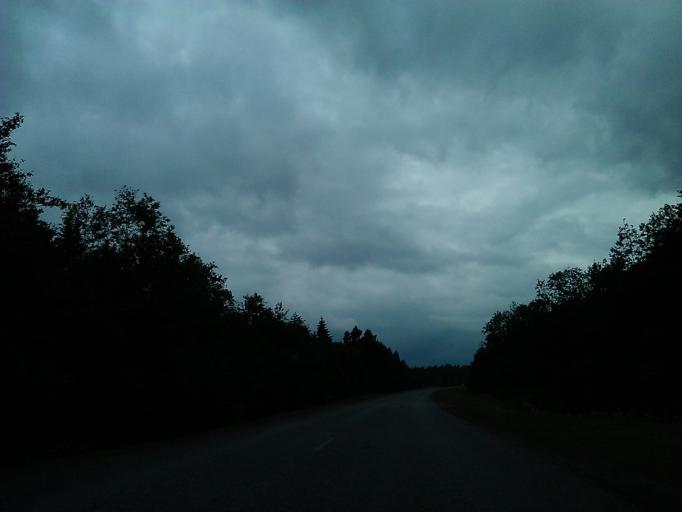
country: LV
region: Kuldigas Rajons
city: Kuldiga
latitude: 56.9865
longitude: 22.0731
